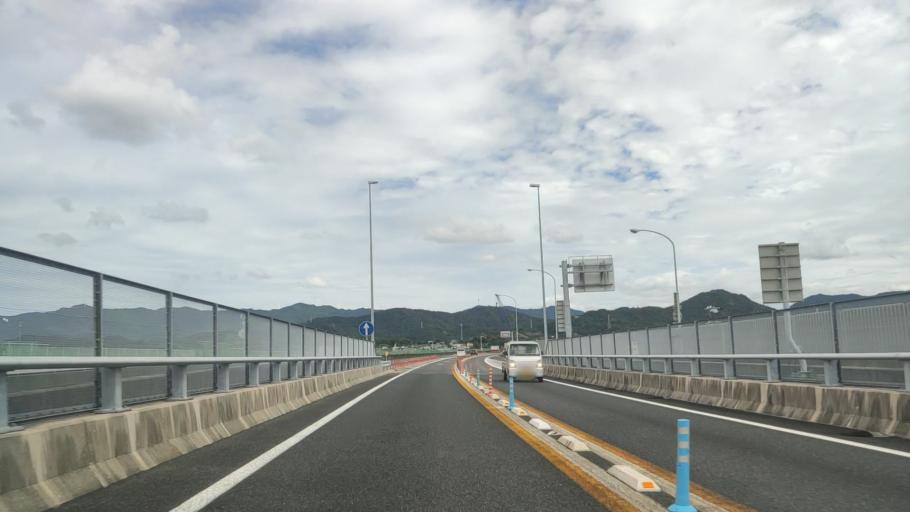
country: JP
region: Wakayama
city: Gobo
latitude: 33.8998
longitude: 135.1856
